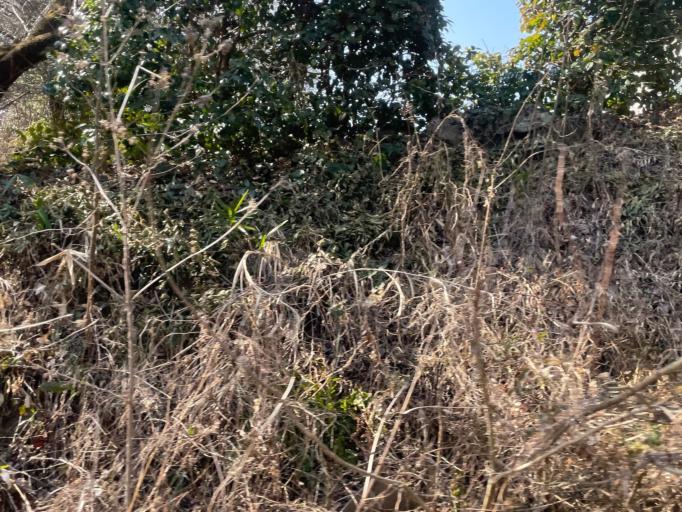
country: JP
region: Gunma
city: Nakanojomachi
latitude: 36.5848
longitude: 138.8629
